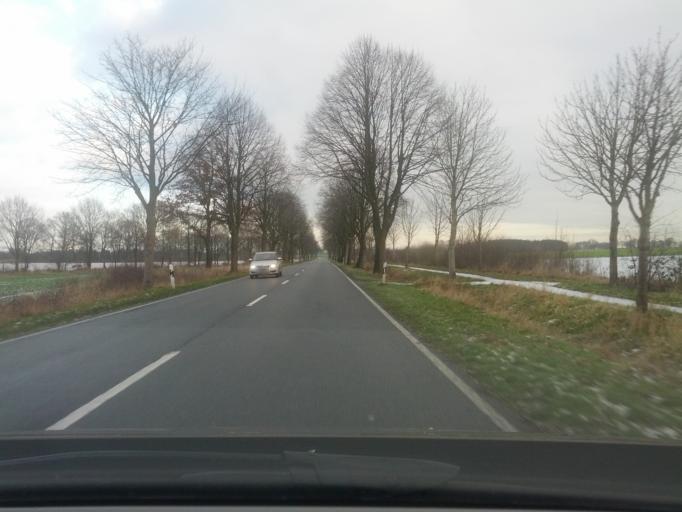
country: DE
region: Lower Saxony
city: Sauensiek
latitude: 53.3918
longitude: 9.6051
